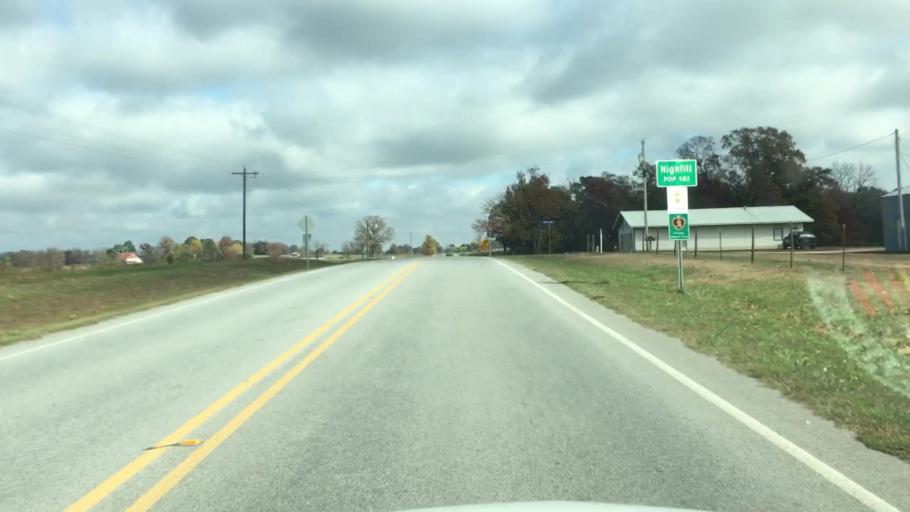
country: US
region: Arkansas
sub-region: Benton County
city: Gentry
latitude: 36.2596
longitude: -94.3715
